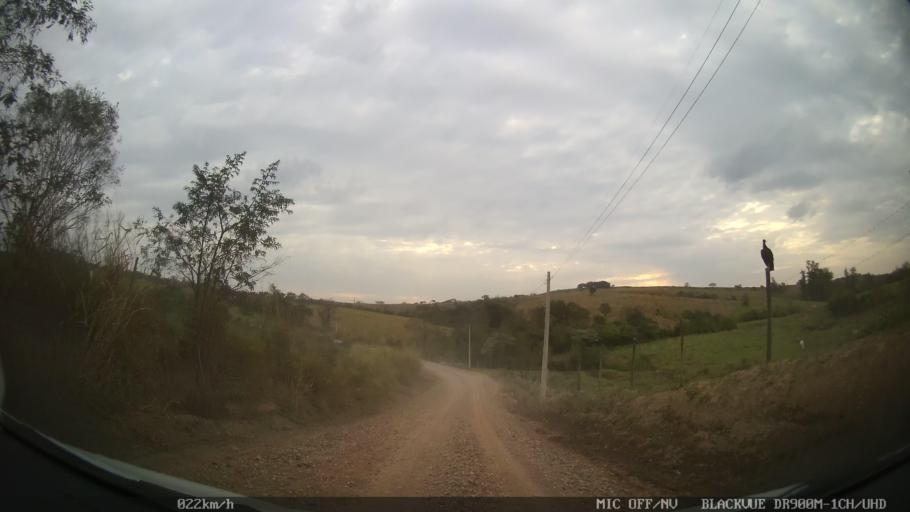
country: BR
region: Sao Paulo
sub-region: Americana
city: Americana
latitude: -22.6788
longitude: -47.3778
